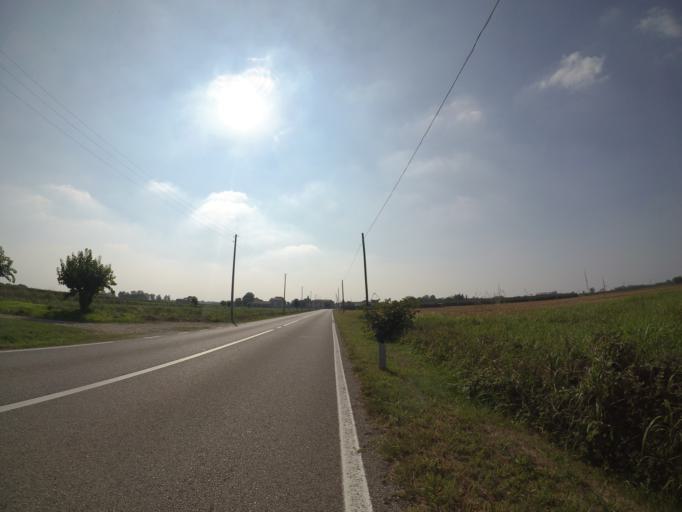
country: IT
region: Friuli Venezia Giulia
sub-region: Provincia di Udine
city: Basiliano
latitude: 45.9995
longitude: 13.0362
